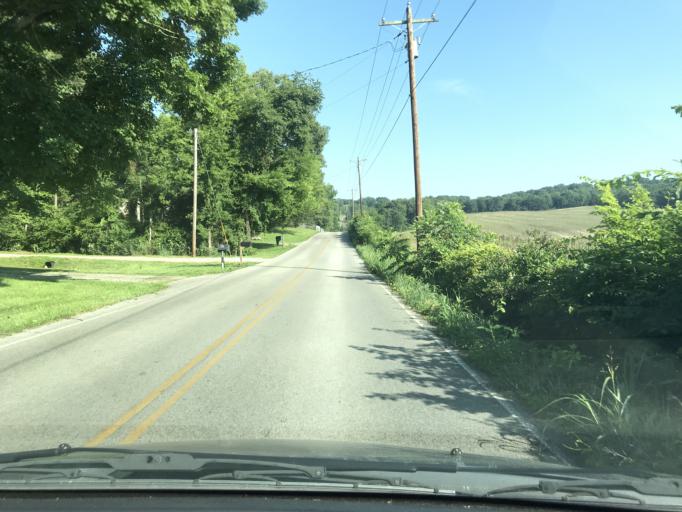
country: US
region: Tennessee
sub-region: Loudon County
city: Loudon
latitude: 35.7791
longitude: -84.3544
